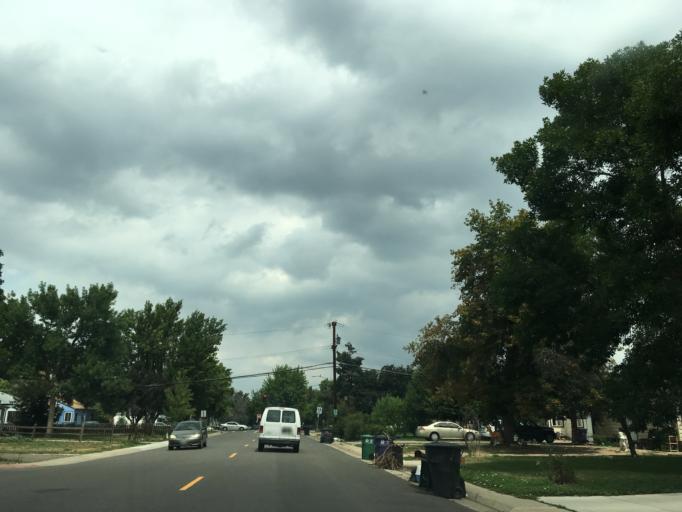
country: US
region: Colorado
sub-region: Arapahoe County
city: Sheridan
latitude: 39.6771
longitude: -105.0298
